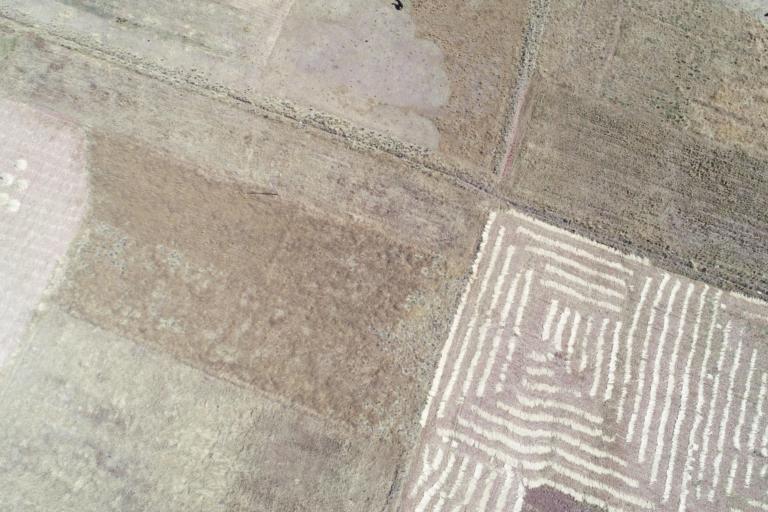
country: BO
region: La Paz
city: Tiahuanaco
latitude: -16.5956
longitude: -68.7752
